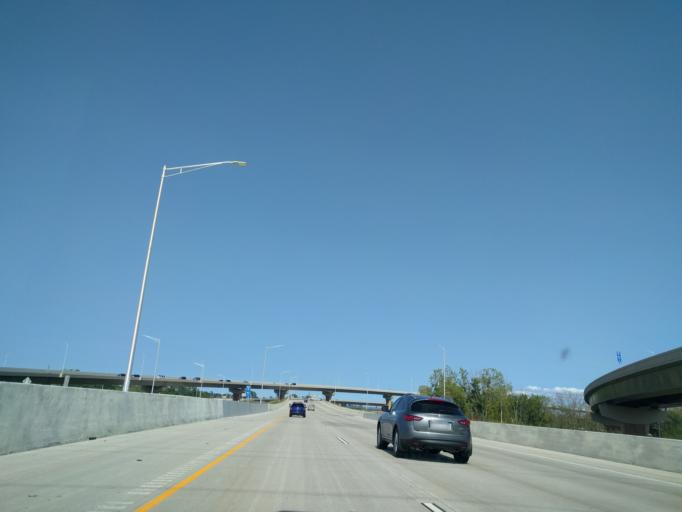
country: US
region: Wisconsin
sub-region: Brown County
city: Howard
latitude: 44.5586
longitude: -88.0573
